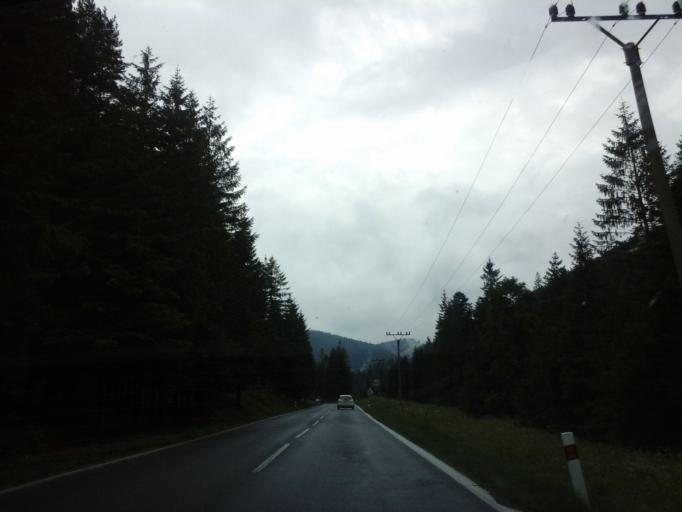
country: SK
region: Presovsky
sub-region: Okres Poprad
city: Zdiar
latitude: 49.2347
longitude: 20.3135
